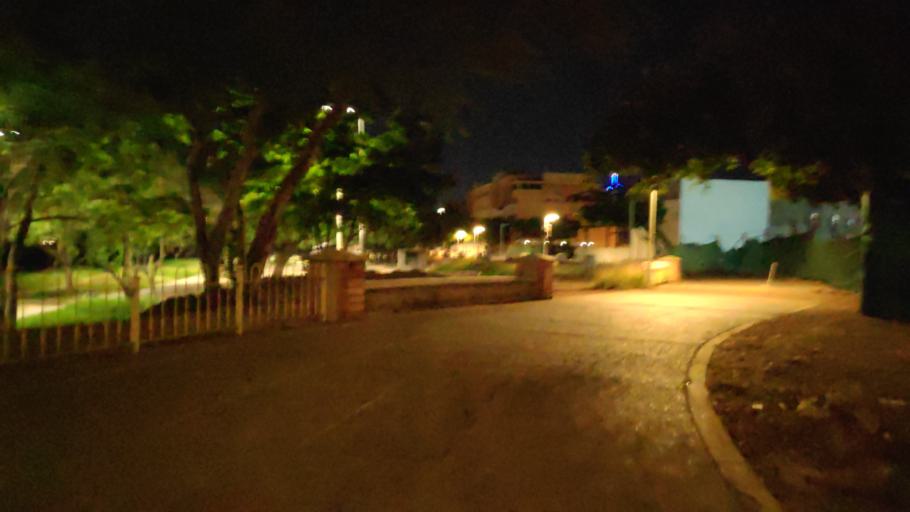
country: MX
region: Sinaloa
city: Culiacan
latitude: 24.8139
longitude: -107.3919
